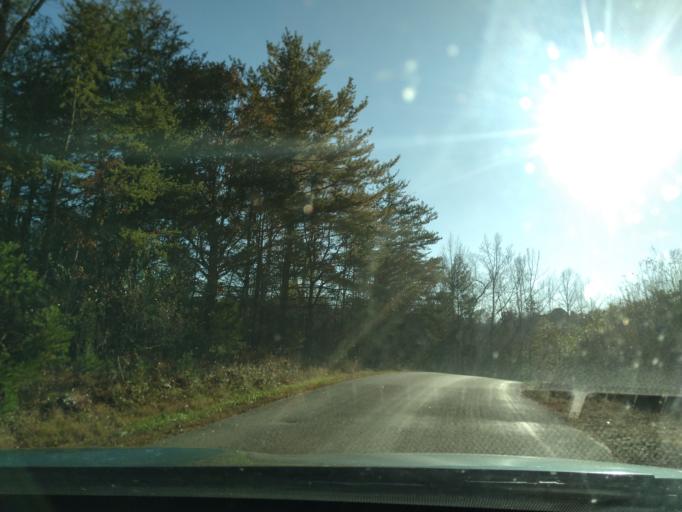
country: US
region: Virginia
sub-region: Floyd County
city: Floyd
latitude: 36.8241
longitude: -80.2127
